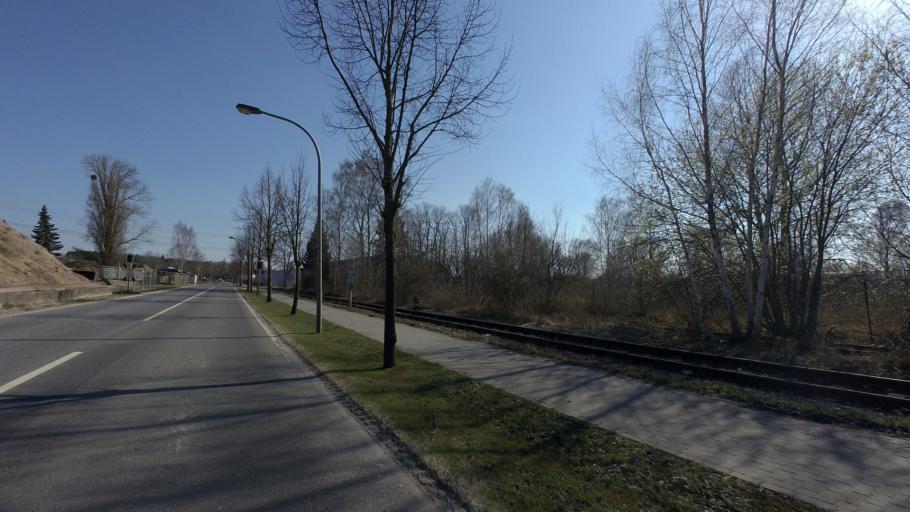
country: DE
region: Brandenburg
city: Velten
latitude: 52.6787
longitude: 13.1970
